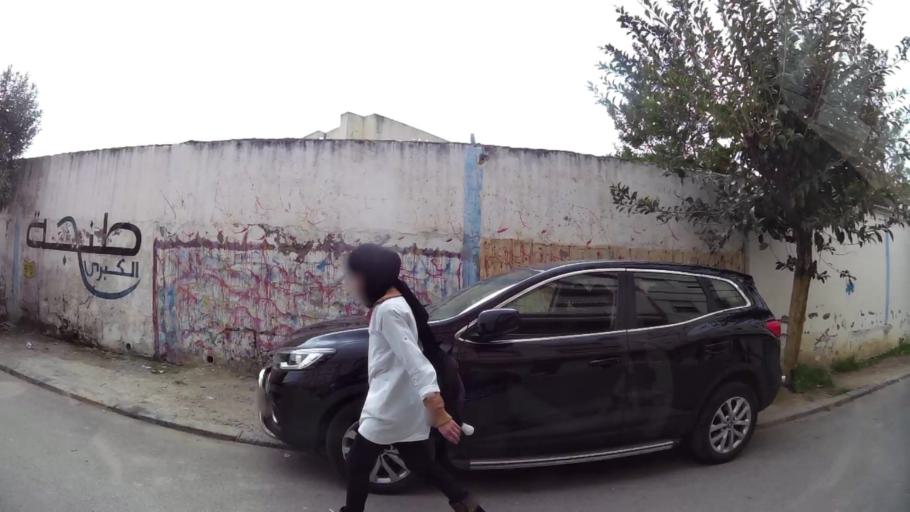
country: MA
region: Tanger-Tetouan
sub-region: Tanger-Assilah
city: Tangier
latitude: 35.7602
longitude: -5.7978
